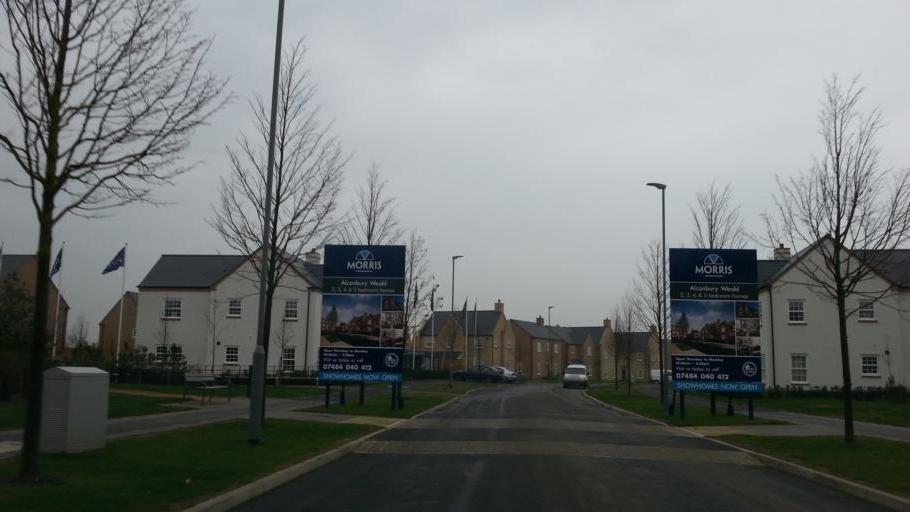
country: GB
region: England
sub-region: Cambridgeshire
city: Great Stukeley
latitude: 52.3703
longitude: -0.2354
